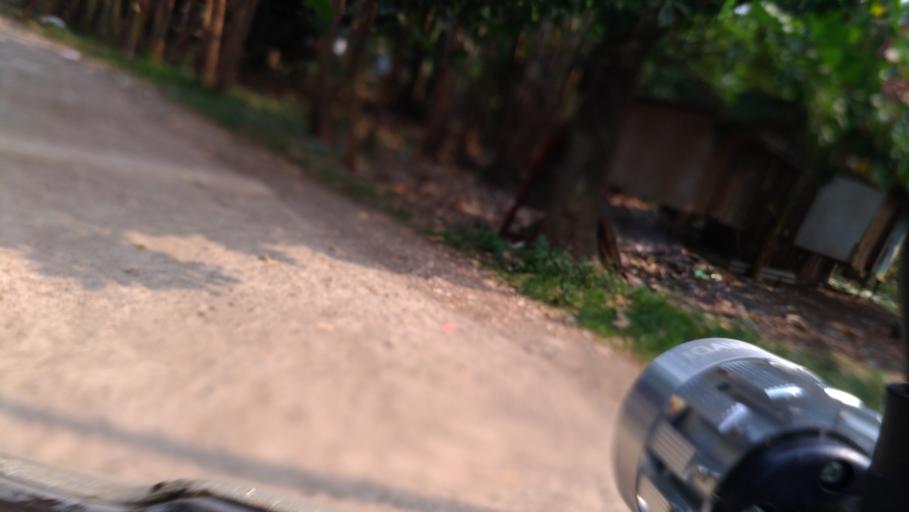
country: ID
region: West Java
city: Depok
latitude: -6.3669
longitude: 106.8767
